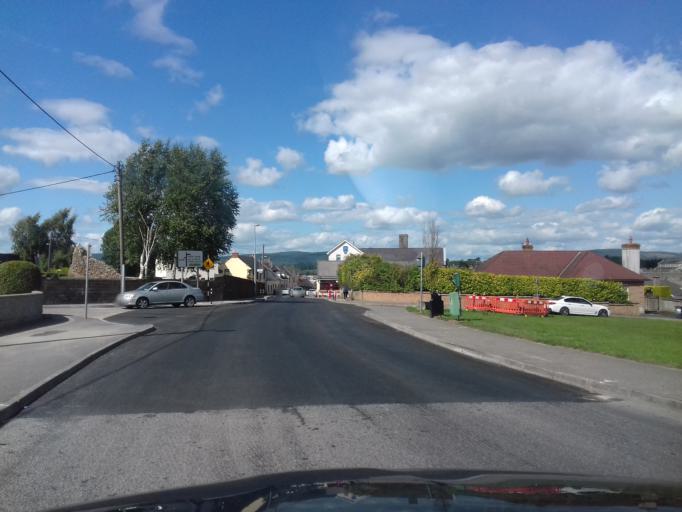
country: IE
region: Munster
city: Carrick-on-Suir
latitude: 52.3423
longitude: -7.4161
